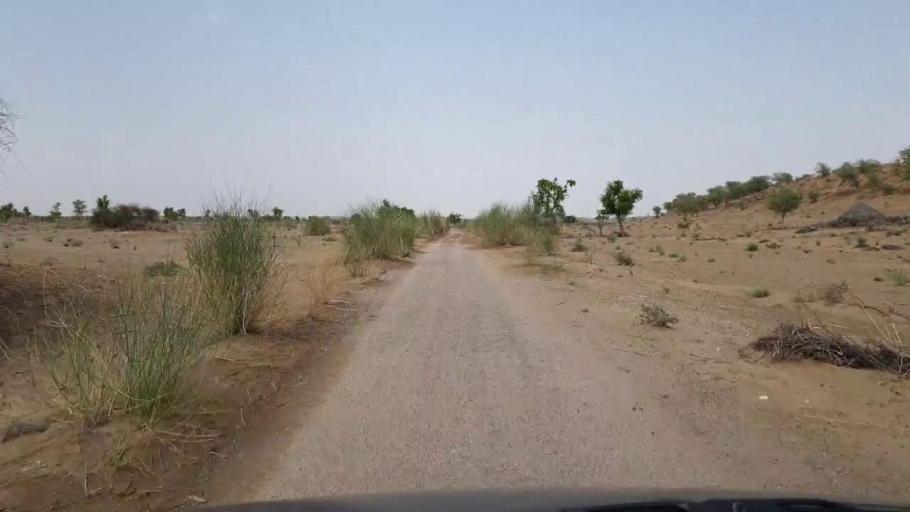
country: PK
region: Sindh
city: Chor
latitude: 25.4753
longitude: 70.5258
